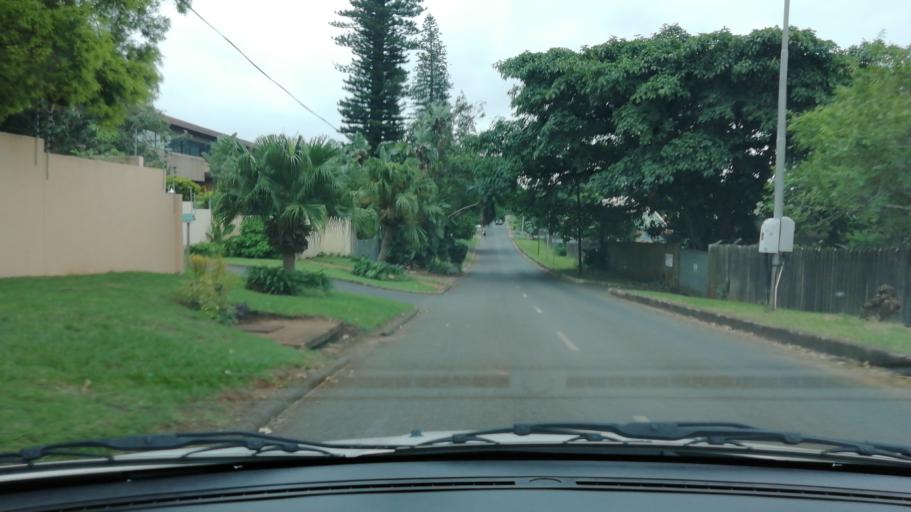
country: ZA
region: KwaZulu-Natal
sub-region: uThungulu District Municipality
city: Empangeni
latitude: -28.7451
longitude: 31.8939
